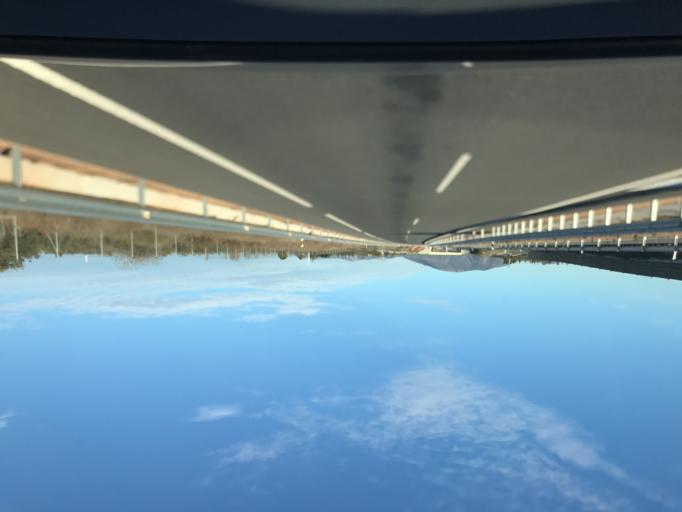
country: ES
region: Andalusia
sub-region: Provincia de Granada
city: Albolote
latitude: 37.2414
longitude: -3.6620
